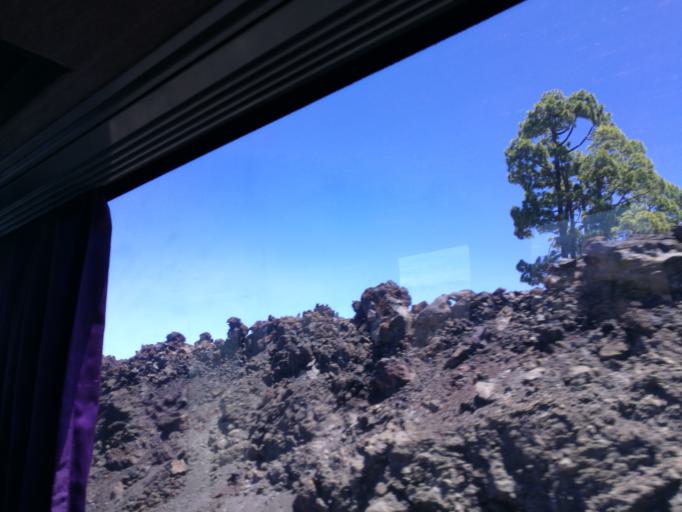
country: ES
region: Canary Islands
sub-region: Provincia de Santa Cruz de Tenerife
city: Guia de Isora
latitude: 28.2743
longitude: -16.7287
